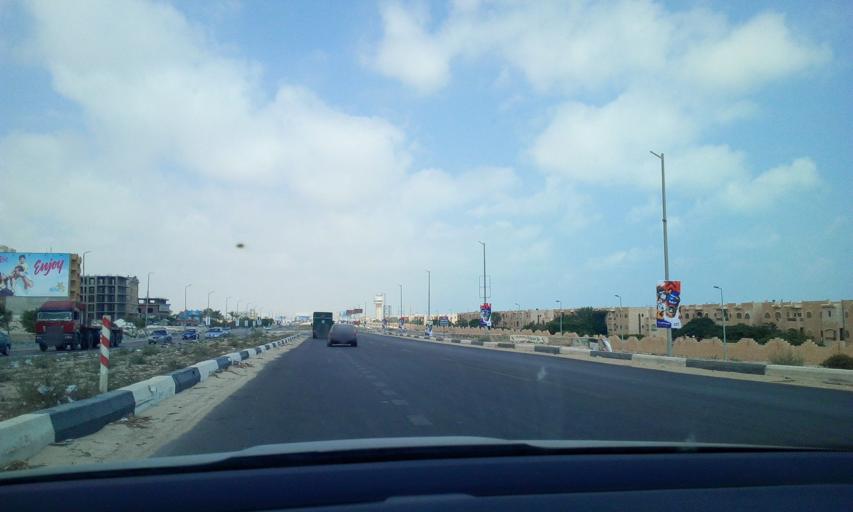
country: EG
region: Muhafazat Matruh
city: Al `Alamayn
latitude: 30.8376
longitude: 28.9560
